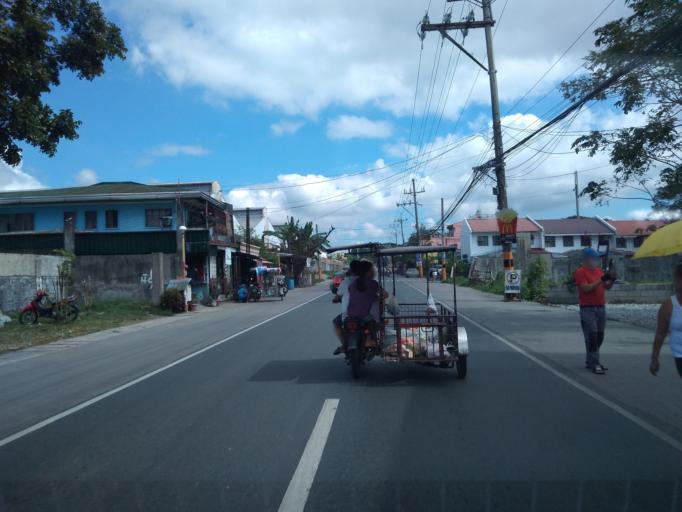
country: PH
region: Central Luzon
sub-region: Province of Bulacan
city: Guyong
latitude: 14.8320
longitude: 120.9740
